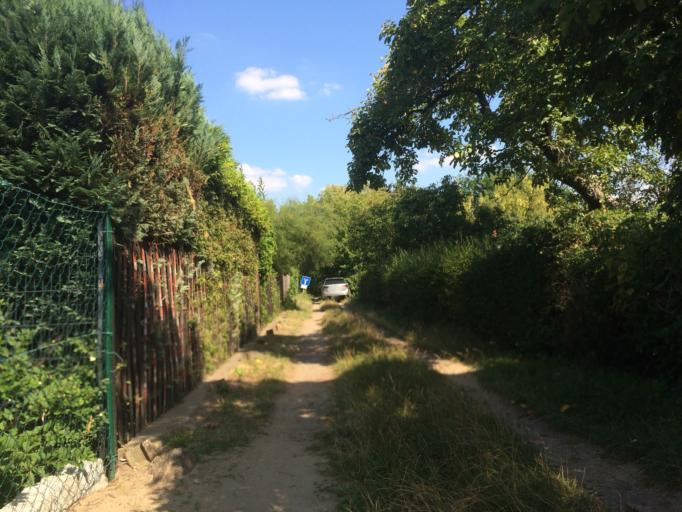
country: DE
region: Berlin
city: Buchholz
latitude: 52.5937
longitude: 13.4165
